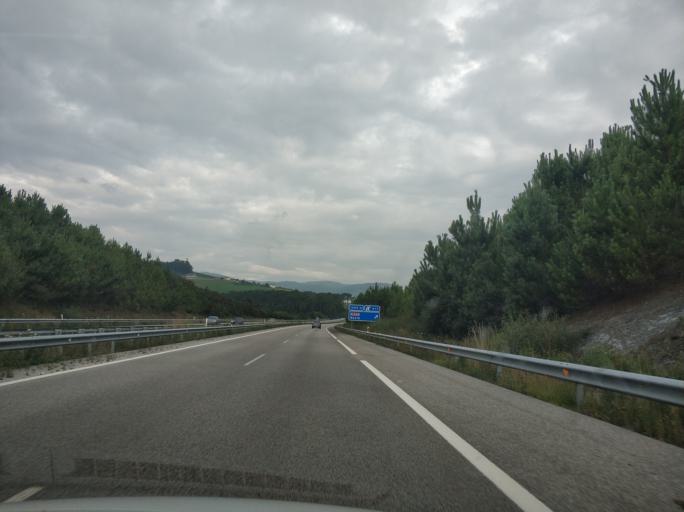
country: ES
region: Asturias
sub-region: Province of Asturias
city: Navia
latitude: 43.5338
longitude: -6.6743
